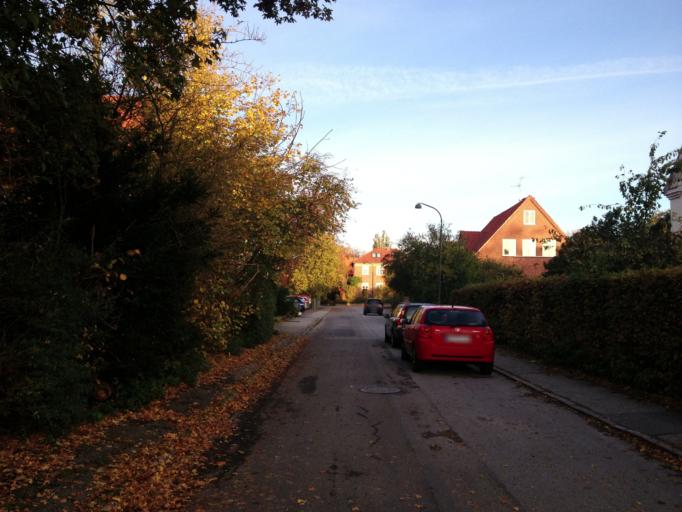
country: SE
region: Skane
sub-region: Lunds Kommun
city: Lund
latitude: 55.7064
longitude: 13.2059
